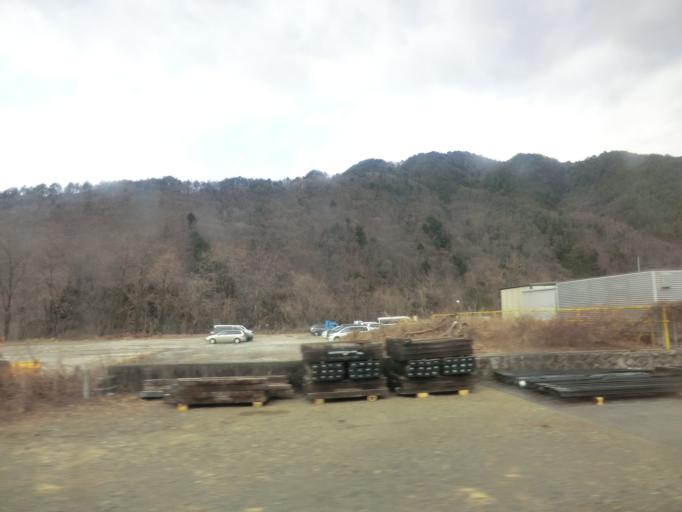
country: JP
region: Nagano
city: Ina
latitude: 35.8412
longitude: 137.6914
